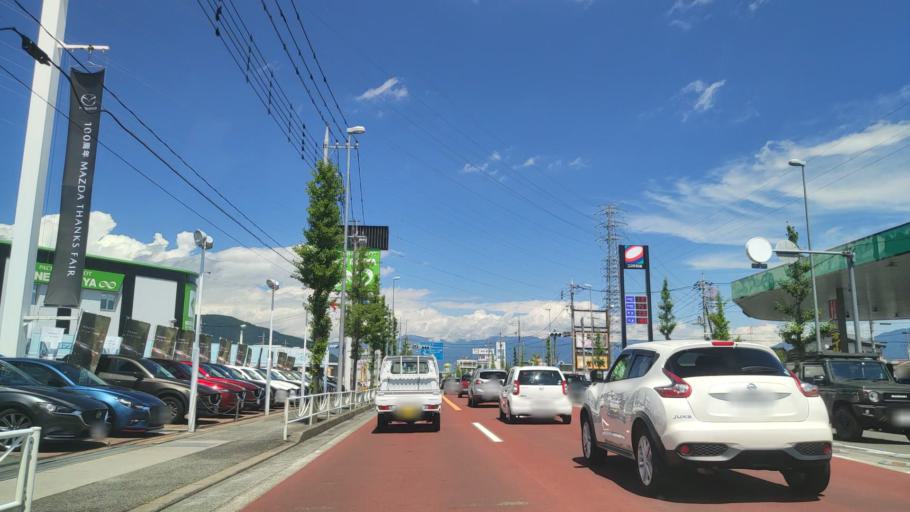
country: JP
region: Yamanashi
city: Kofu-shi
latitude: 35.6357
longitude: 138.5809
